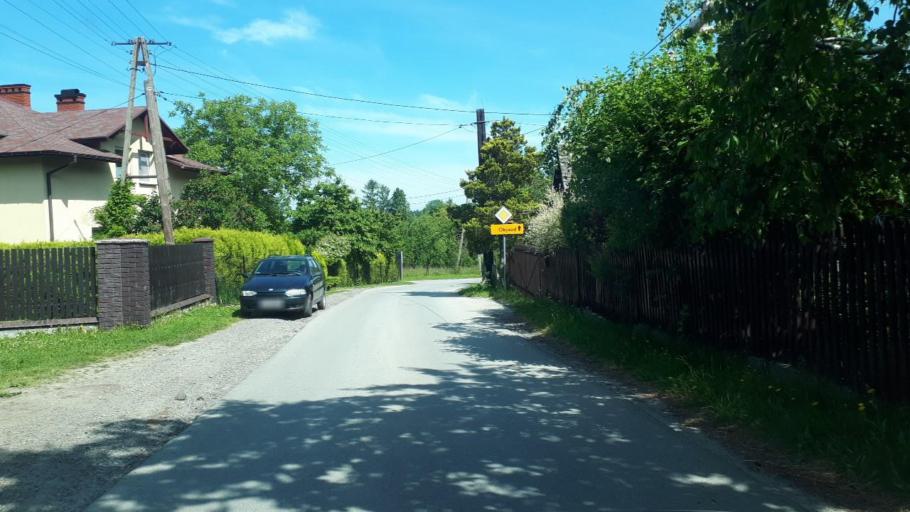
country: PL
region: Silesian Voivodeship
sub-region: Powiat bielski
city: Jaworze
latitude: 49.7864
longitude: 18.9453
